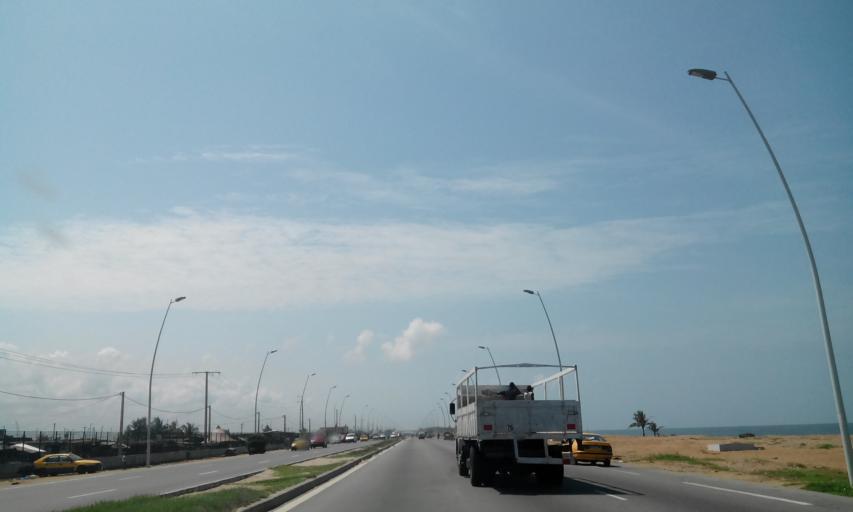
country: CI
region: Lagunes
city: Bingerville
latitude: 5.2420
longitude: -3.9139
